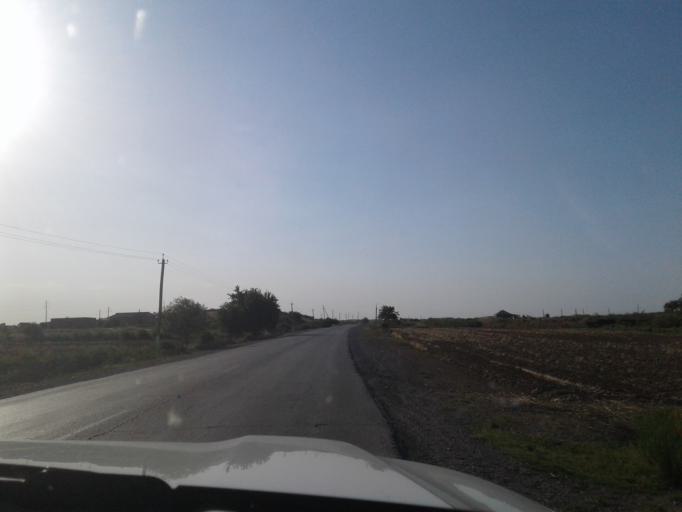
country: TM
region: Mary
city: Yoloeten
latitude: 37.2105
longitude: 62.3846
